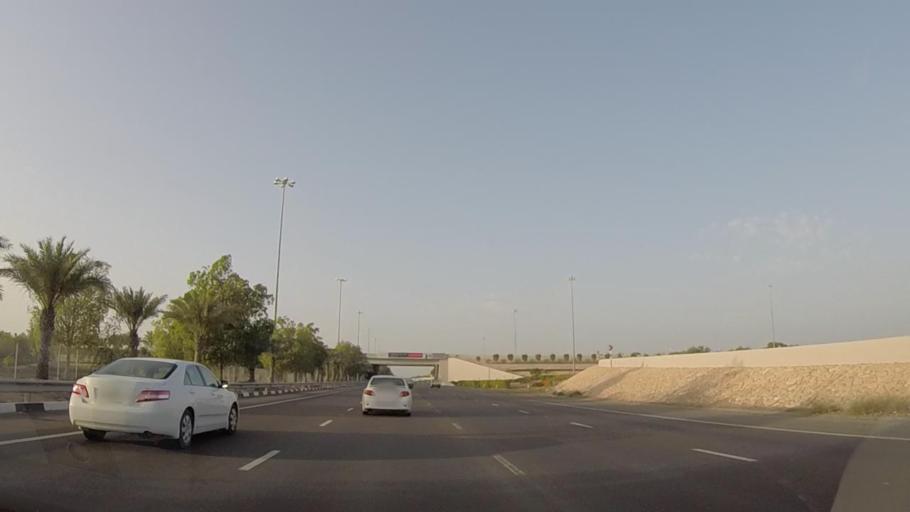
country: AE
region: Dubai
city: Dubai
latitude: 24.8616
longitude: 54.9077
